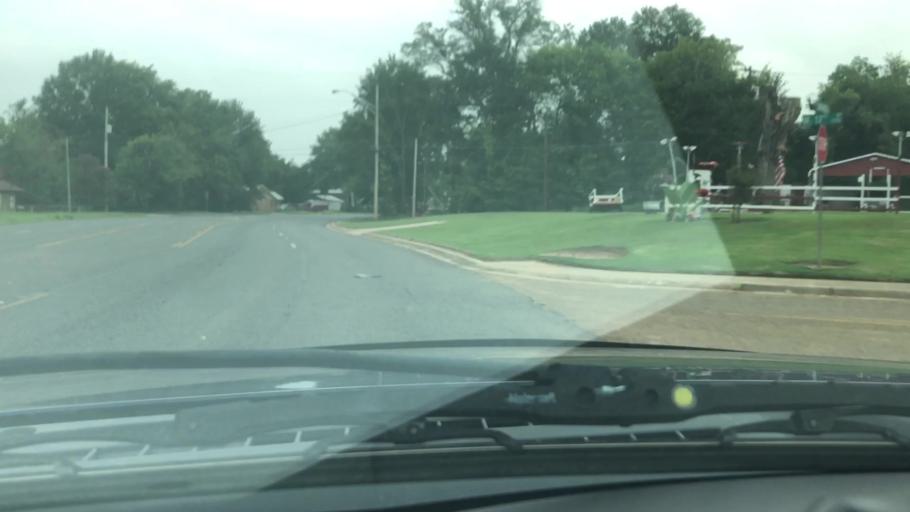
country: US
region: Texas
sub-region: Bowie County
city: Texarkana
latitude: 33.4327
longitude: -94.0620
